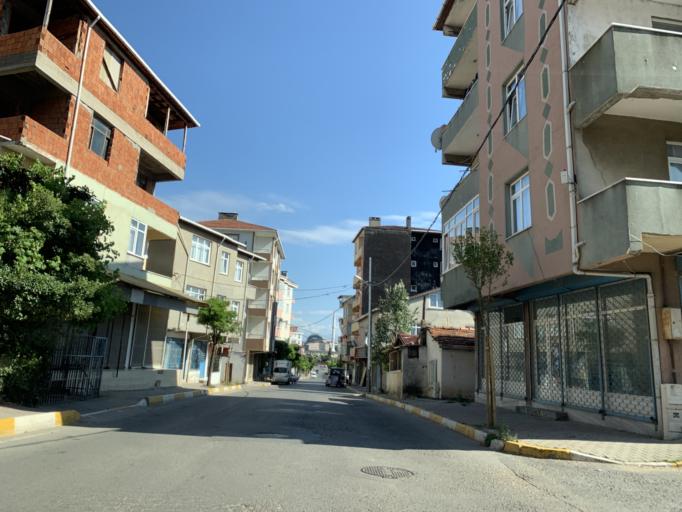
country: TR
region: Istanbul
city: Pendik
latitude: 40.8839
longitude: 29.2795
